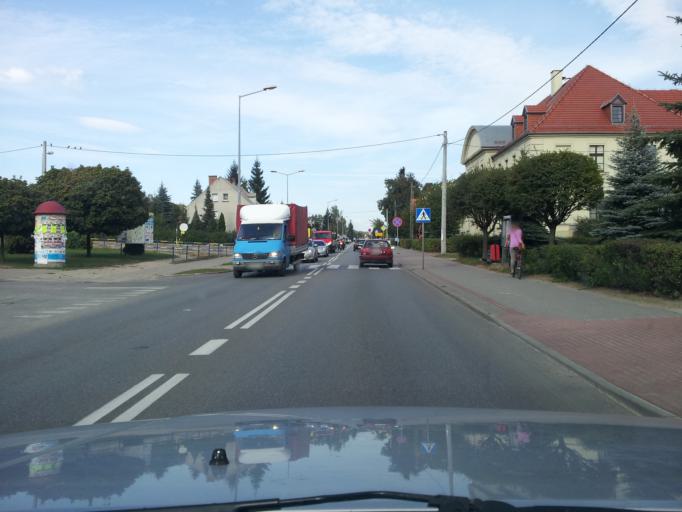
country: PL
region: Warmian-Masurian Voivodeship
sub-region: Powiat nowomiejski
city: Nowe Miasto Lubawskie
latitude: 53.4298
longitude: 19.5894
